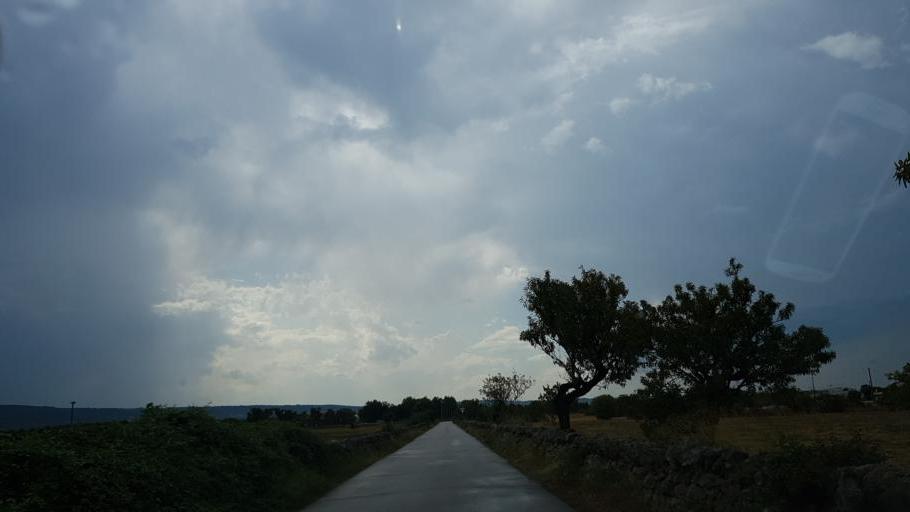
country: IT
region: Apulia
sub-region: Provincia di Bari
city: Monopoli
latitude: 40.9275
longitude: 17.3242
